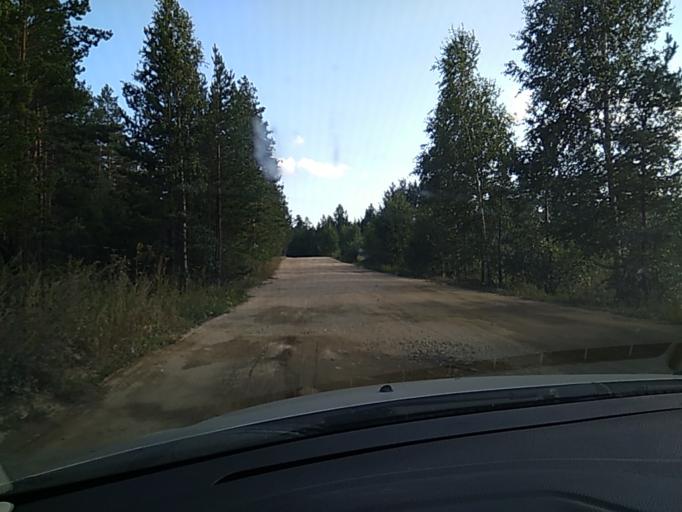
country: RU
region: Chelyabinsk
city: Kyshtym
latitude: 55.6827
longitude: 60.5724
